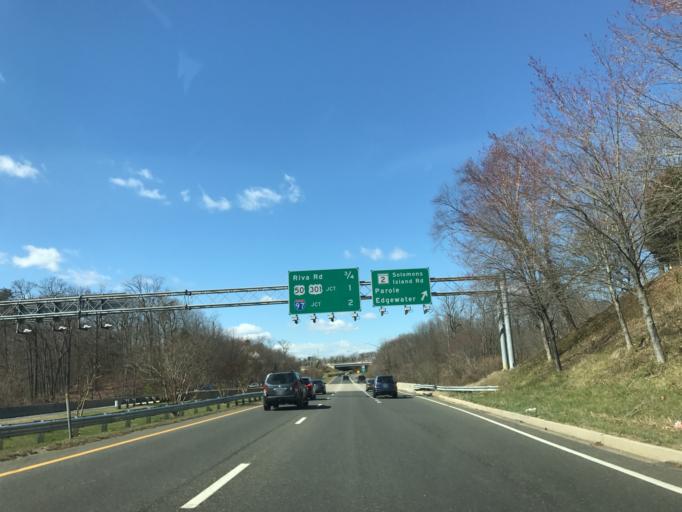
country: US
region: Maryland
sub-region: Anne Arundel County
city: Parole
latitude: 38.9714
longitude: -76.5363
